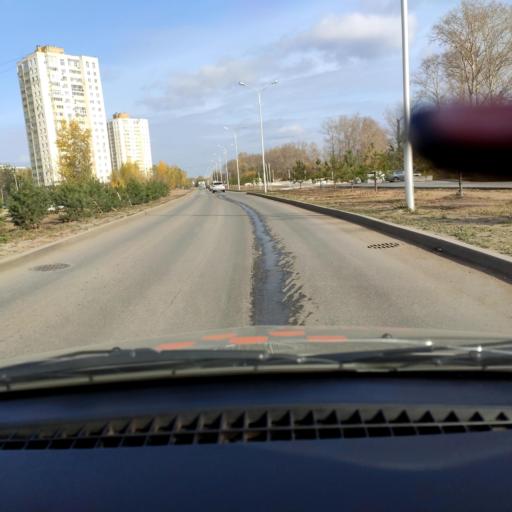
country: RU
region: Bashkortostan
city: Ufa
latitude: 54.7624
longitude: 56.0736
